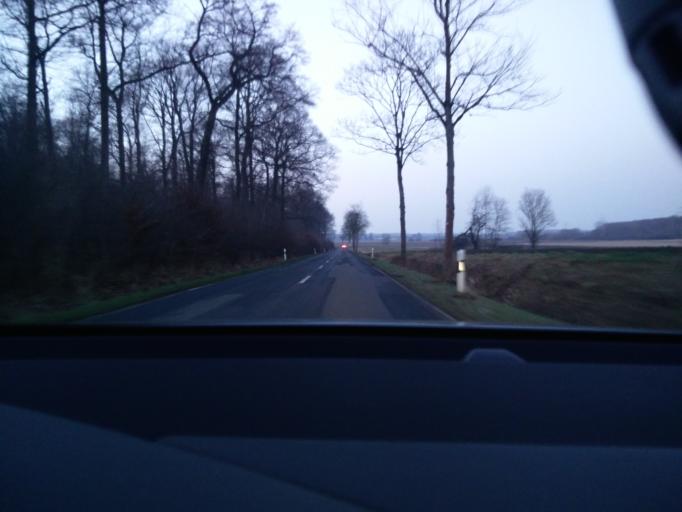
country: DE
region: Lower Saxony
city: Laatzen
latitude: 52.3125
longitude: 9.8603
